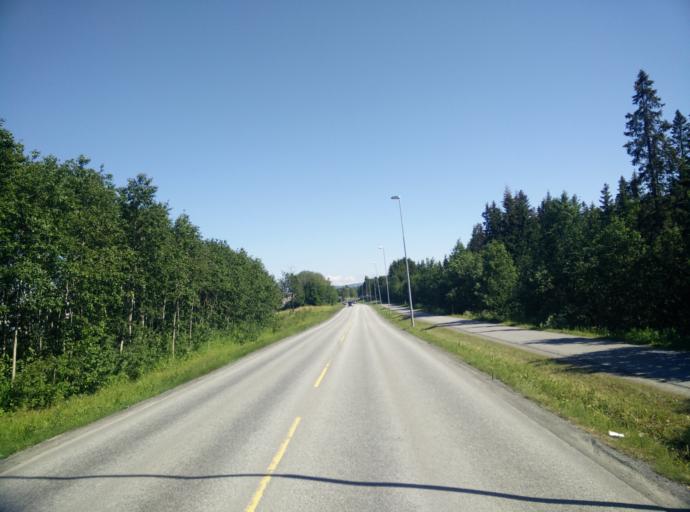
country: NO
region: Sor-Trondelag
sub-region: Trondheim
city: Trondheim
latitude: 63.3726
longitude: 10.3334
